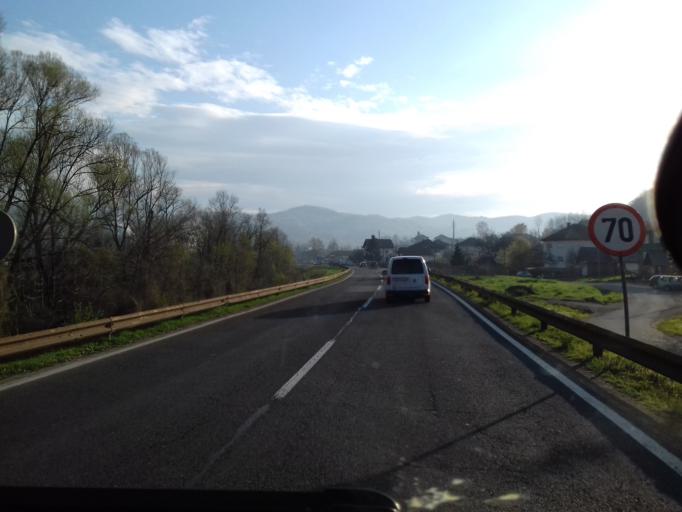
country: BA
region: Federation of Bosnia and Herzegovina
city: Maglaj
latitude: 44.5209
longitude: 18.0895
